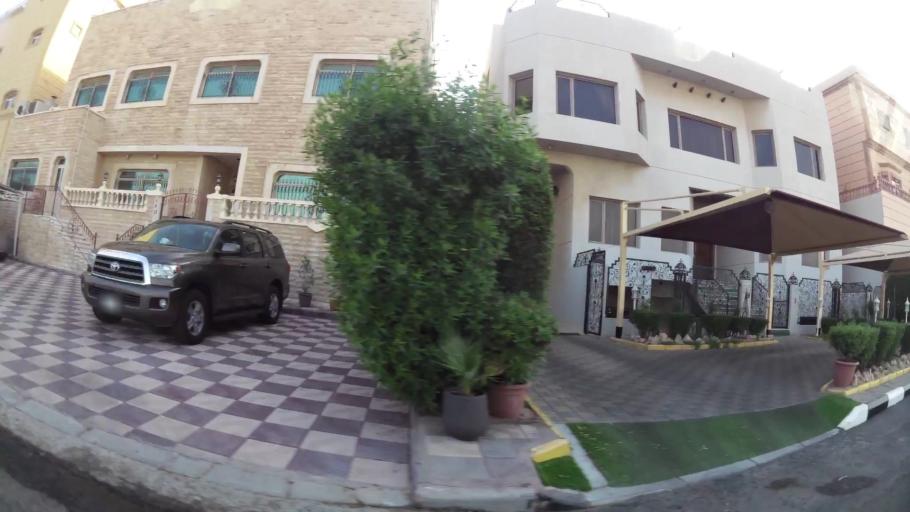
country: KW
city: Al Funaytis
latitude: 29.2310
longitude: 48.0800
